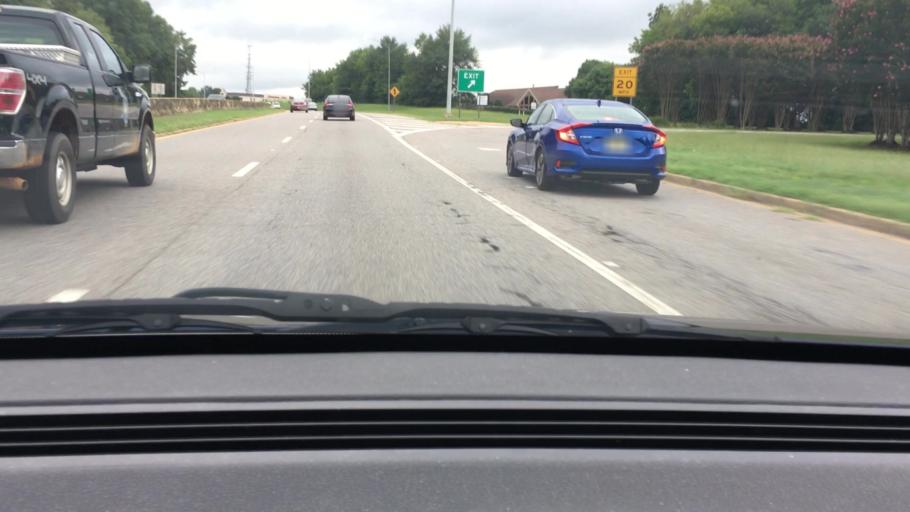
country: US
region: Alabama
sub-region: Tuscaloosa County
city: Tuscaloosa
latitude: 33.2068
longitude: -87.5244
